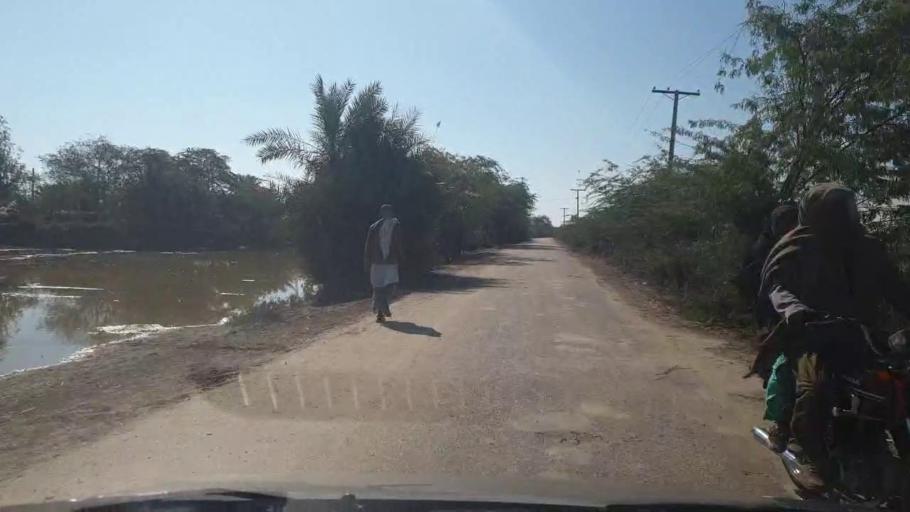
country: PK
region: Sindh
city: Bozdar
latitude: 27.1306
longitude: 68.6413
